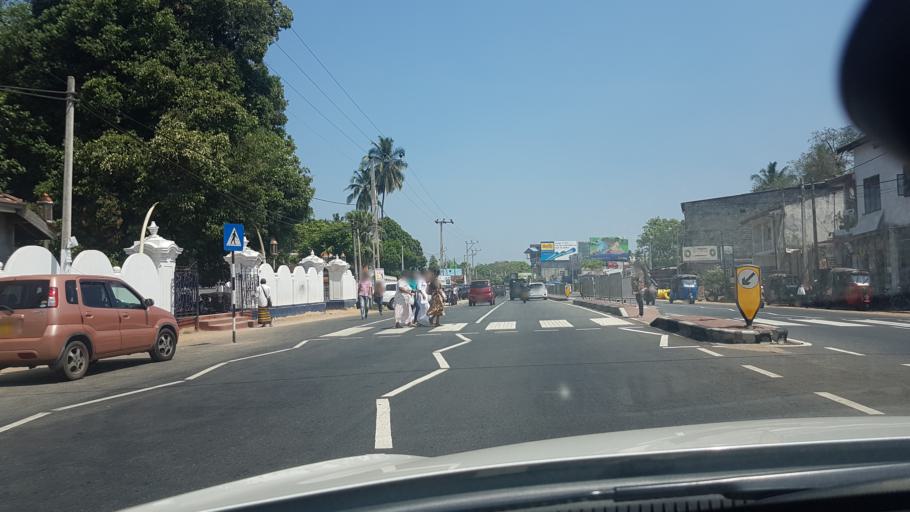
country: LK
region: Western
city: Gampaha
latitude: 7.0941
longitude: 80.0388
